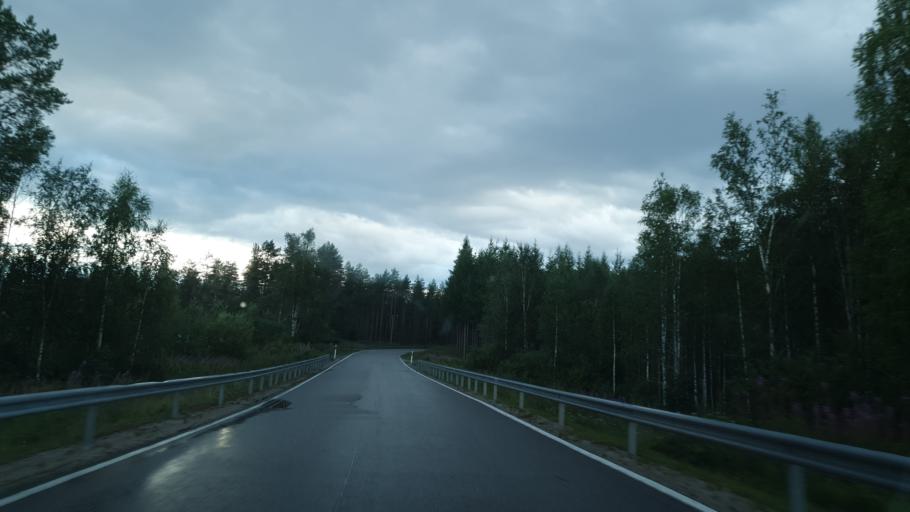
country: FI
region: North Karelia
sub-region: Pielisen Karjala
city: Lieksa
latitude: 63.5371
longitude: 29.9801
